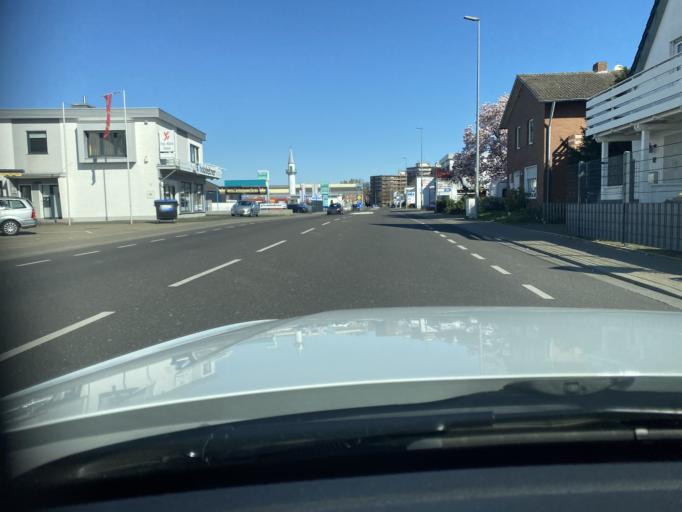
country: DE
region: North Rhine-Westphalia
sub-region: Regierungsbezirk Dusseldorf
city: Grevenbroich
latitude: 51.0870
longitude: 6.5758
